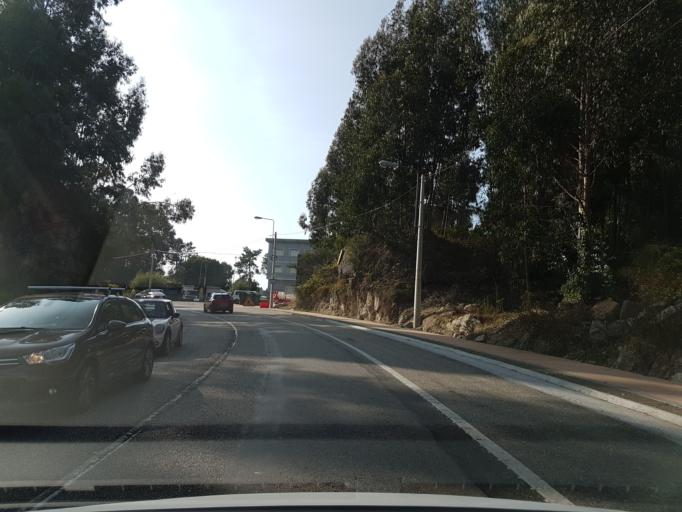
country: ES
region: Galicia
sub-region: Provincia de Pontevedra
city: Nigran
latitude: 42.1866
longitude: -8.7843
